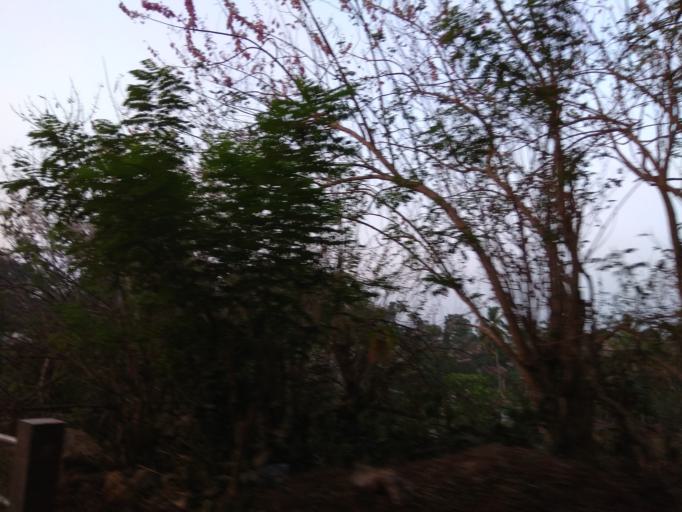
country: IN
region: Karnataka
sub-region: Dakshina Kannada
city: Mangalore
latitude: 12.9332
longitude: 74.8673
